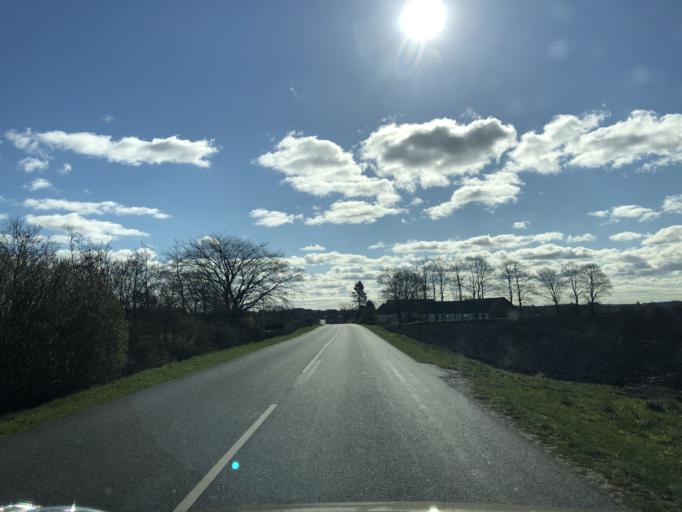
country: DK
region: North Denmark
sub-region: Vesthimmerland Kommune
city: Alestrup
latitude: 56.6158
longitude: 9.5149
